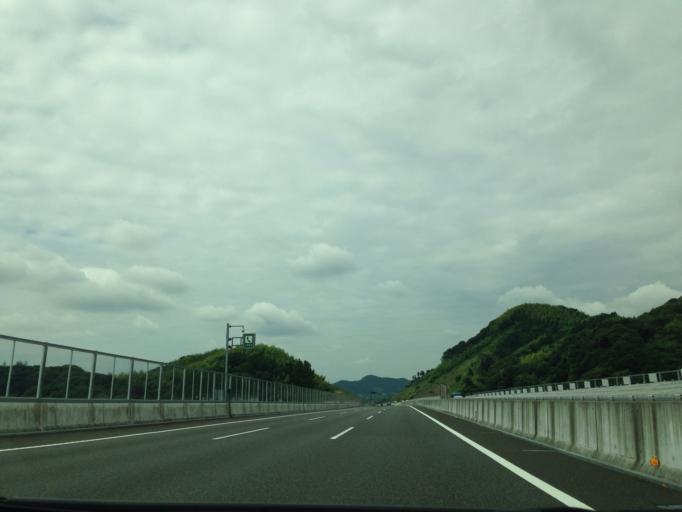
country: JP
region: Shizuoka
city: Fujieda
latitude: 34.9159
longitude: 138.2614
